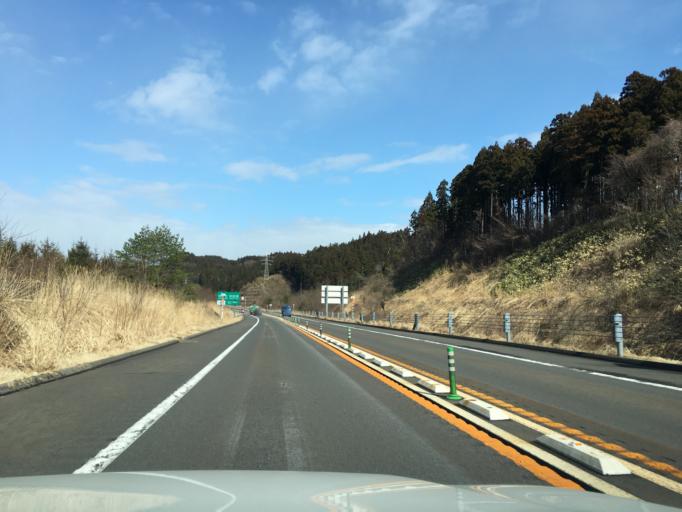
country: JP
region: Akita
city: Akita
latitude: 39.7720
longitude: 140.1206
